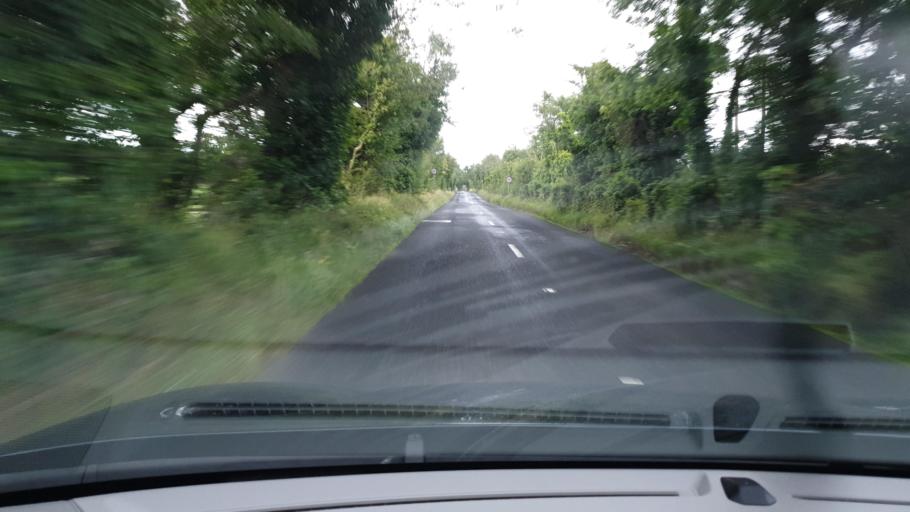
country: IE
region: Leinster
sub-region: South Dublin
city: Rathcoole
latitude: 53.2676
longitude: -6.4907
